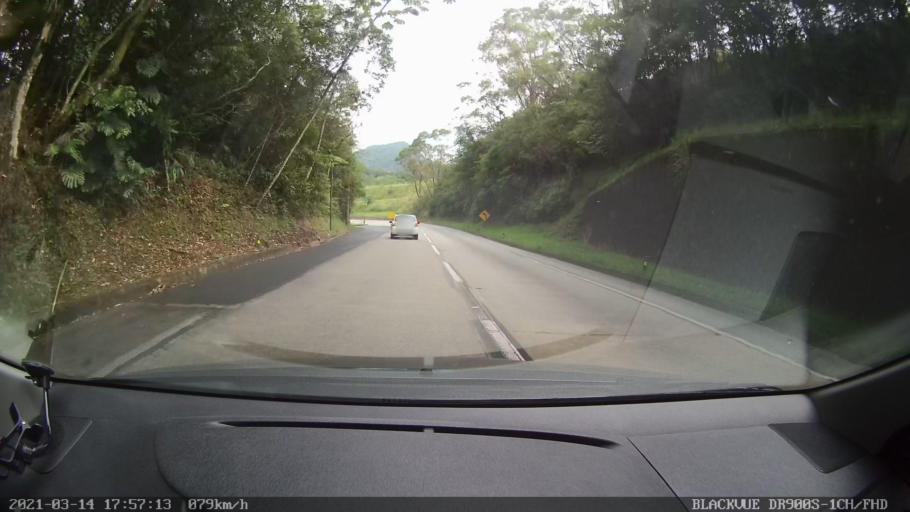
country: BR
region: Rio de Janeiro
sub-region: Petropolis
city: Petropolis
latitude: -22.5154
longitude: -43.2302
